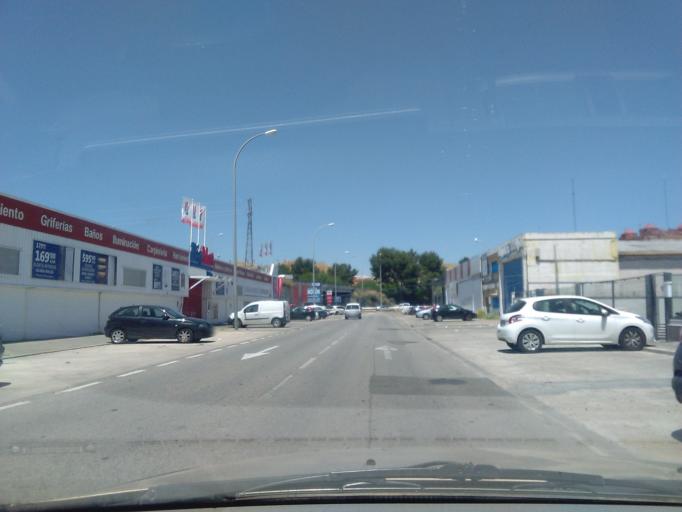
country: ES
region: Andalusia
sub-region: Provincia de Sevilla
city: Sevilla
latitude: 37.3849
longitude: -5.9235
